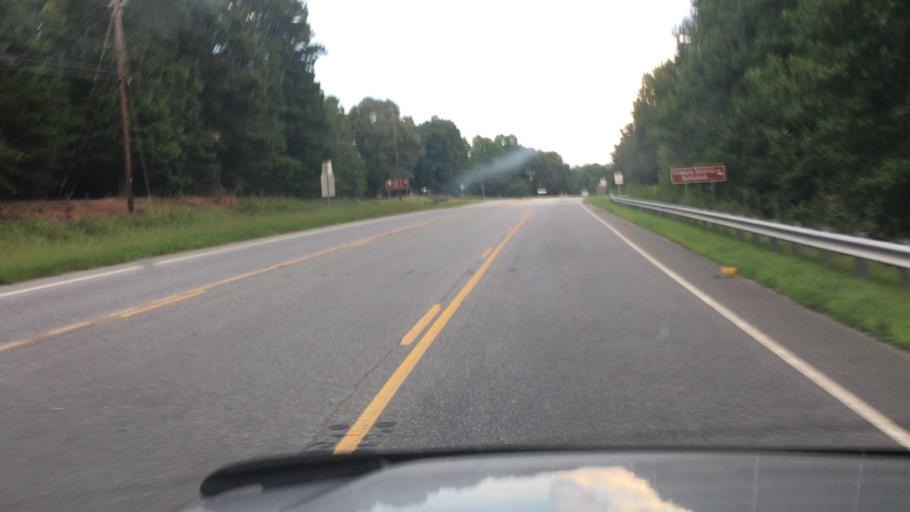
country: US
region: South Carolina
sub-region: Spartanburg County
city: Mayo
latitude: 35.1423
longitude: -81.8173
